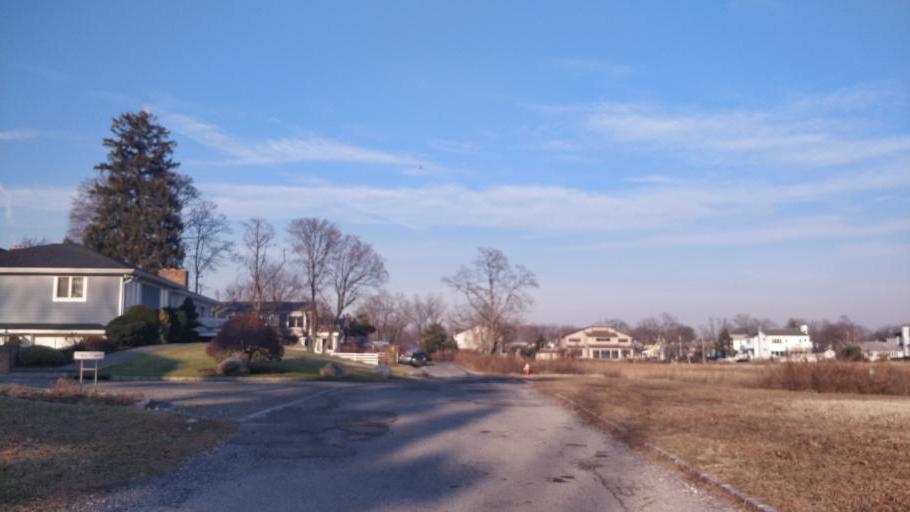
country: US
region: New York
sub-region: Nassau County
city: Bayville
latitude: 40.9059
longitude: -73.5575
